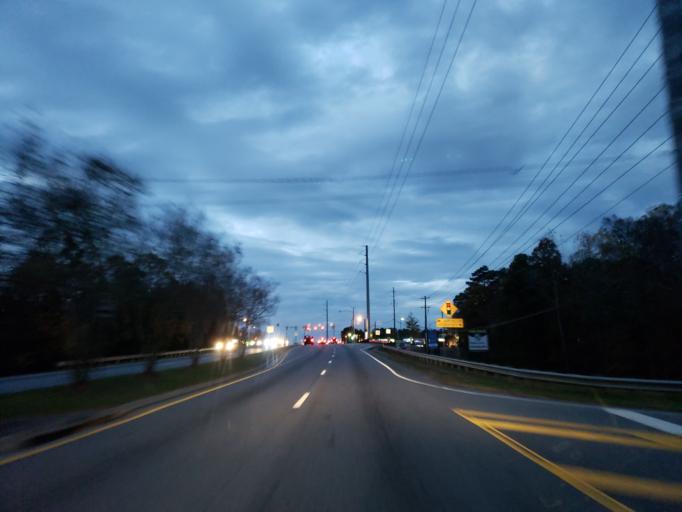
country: US
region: Georgia
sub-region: Cobb County
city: Powder Springs
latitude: 33.9398
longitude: -84.7054
